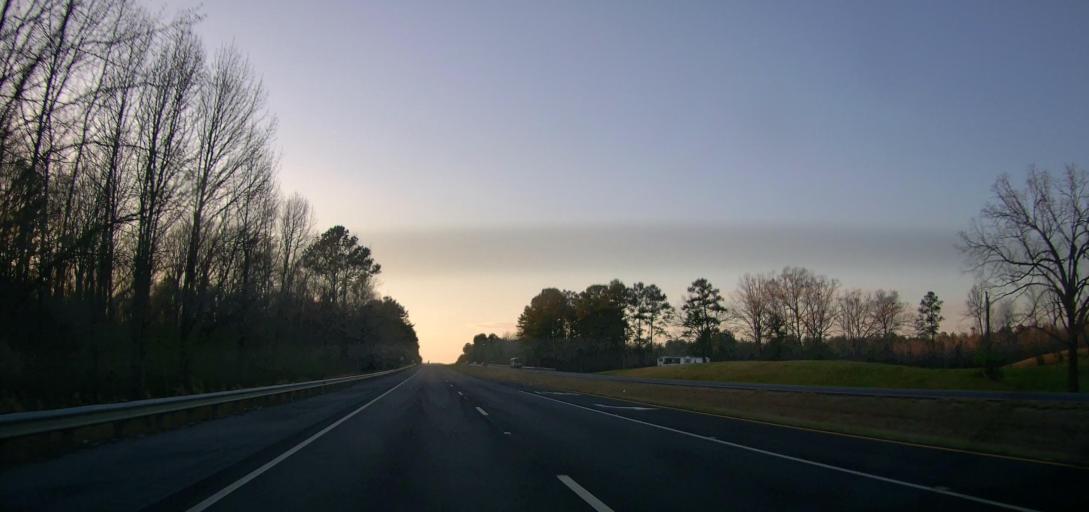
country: US
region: Alabama
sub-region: Coosa County
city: Stewartville
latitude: 33.1027
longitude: -86.2251
